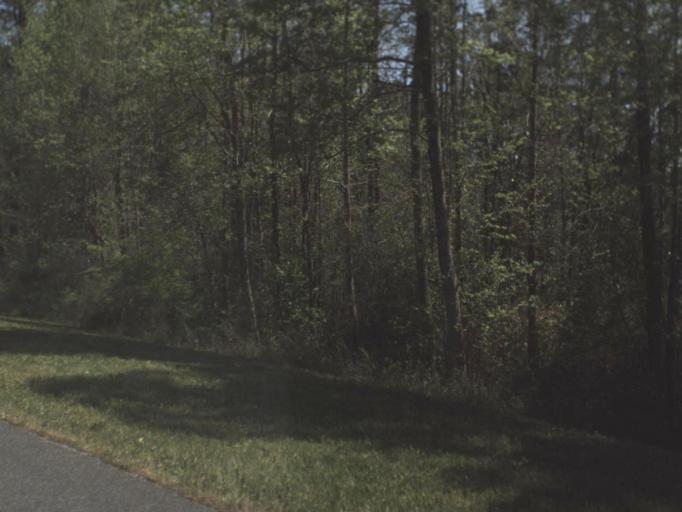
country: US
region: Alabama
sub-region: Escambia County
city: East Brewton
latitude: 30.9517
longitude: -87.0953
